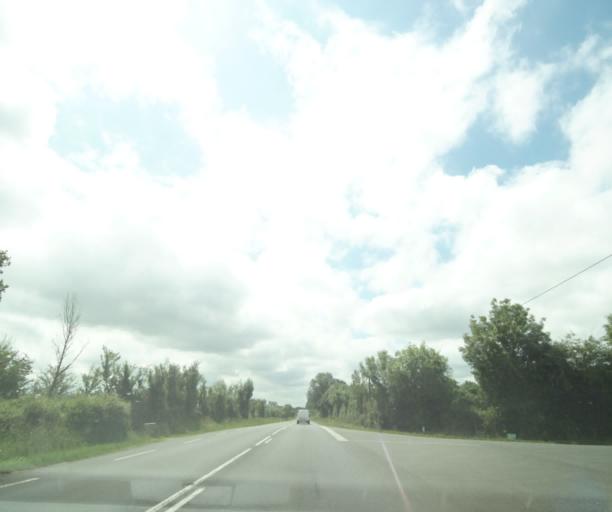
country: FR
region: Poitou-Charentes
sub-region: Departement des Deux-Sevres
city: Viennay
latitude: 46.7245
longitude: -0.2380
